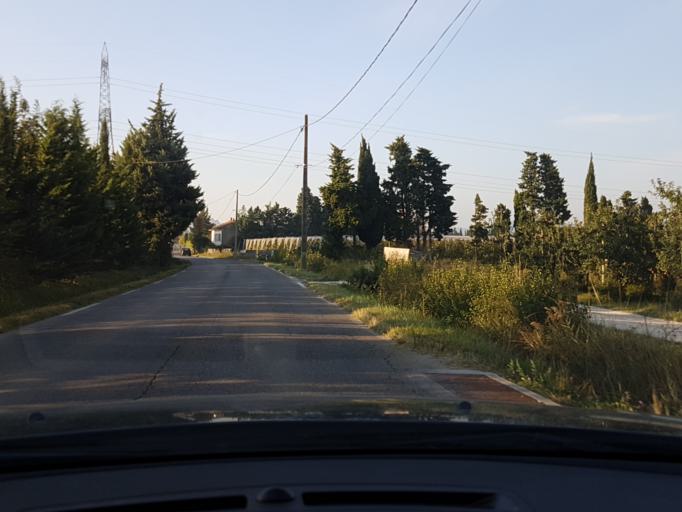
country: FR
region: Provence-Alpes-Cote d'Azur
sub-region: Departement des Bouches-du-Rhone
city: Molleges
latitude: 43.7931
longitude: 4.9544
